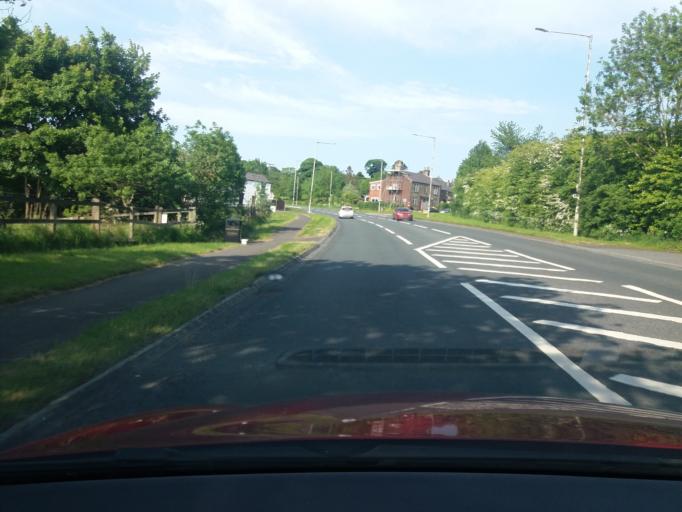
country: GB
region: England
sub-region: Lancashire
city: Chorley
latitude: 53.6846
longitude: -2.6024
